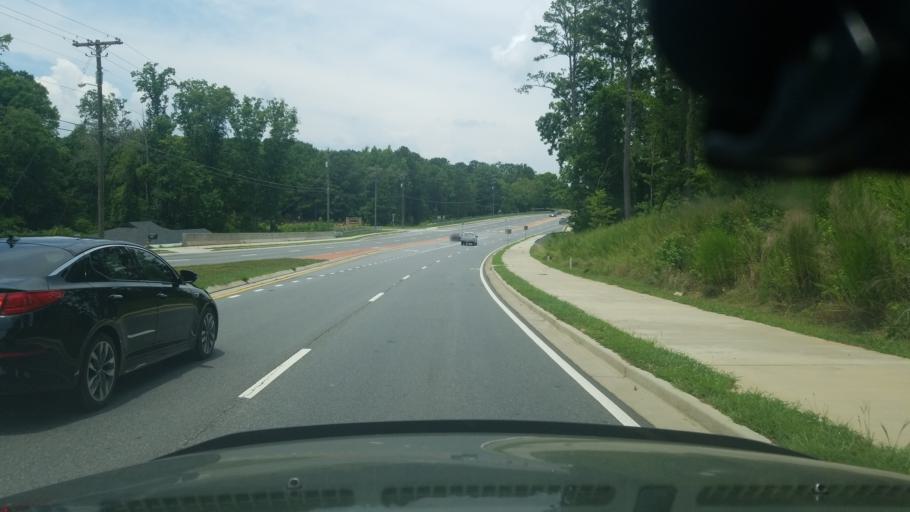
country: US
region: Georgia
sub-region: Fulton County
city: Milton
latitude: 34.1358
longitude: -84.2291
